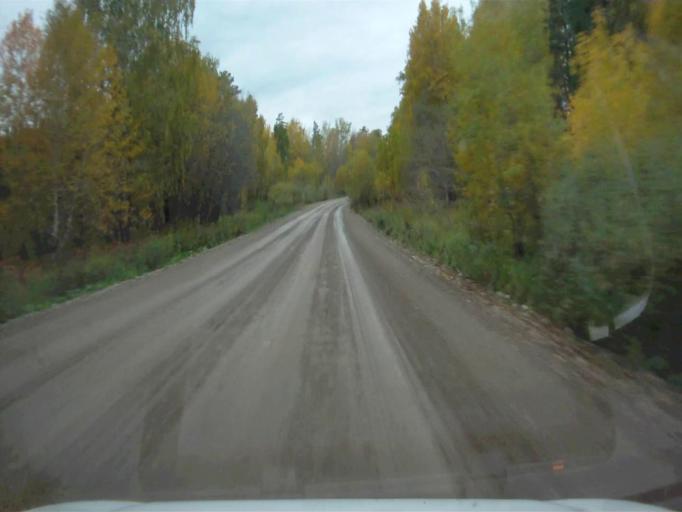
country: RU
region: Chelyabinsk
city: Nyazepetrovsk
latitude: 56.1096
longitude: 59.3749
